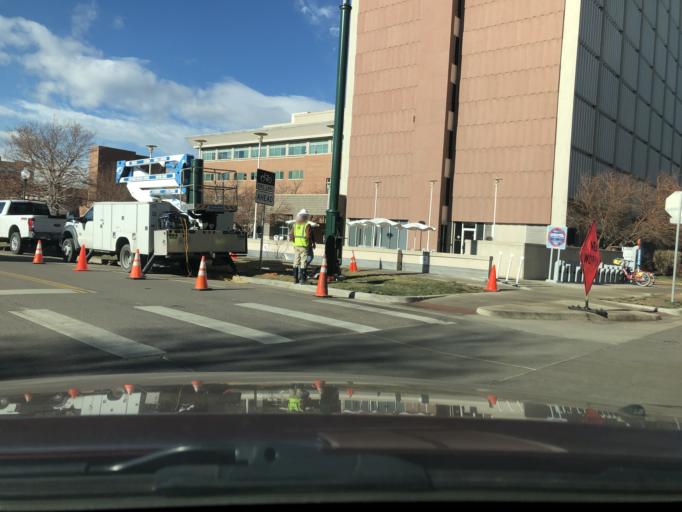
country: US
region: Colorado
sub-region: Denver County
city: Denver
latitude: 39.7470
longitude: -104.9685
